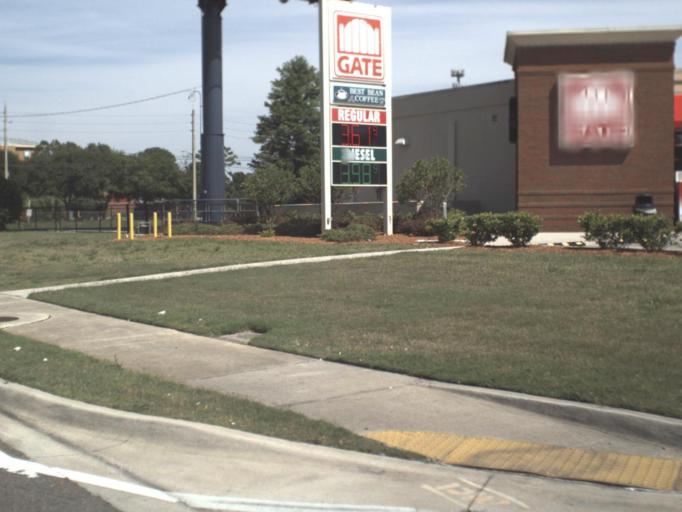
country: US
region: Florida
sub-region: Saint Johns County
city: Fruit Cove
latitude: 30.2208
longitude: -81.5686
